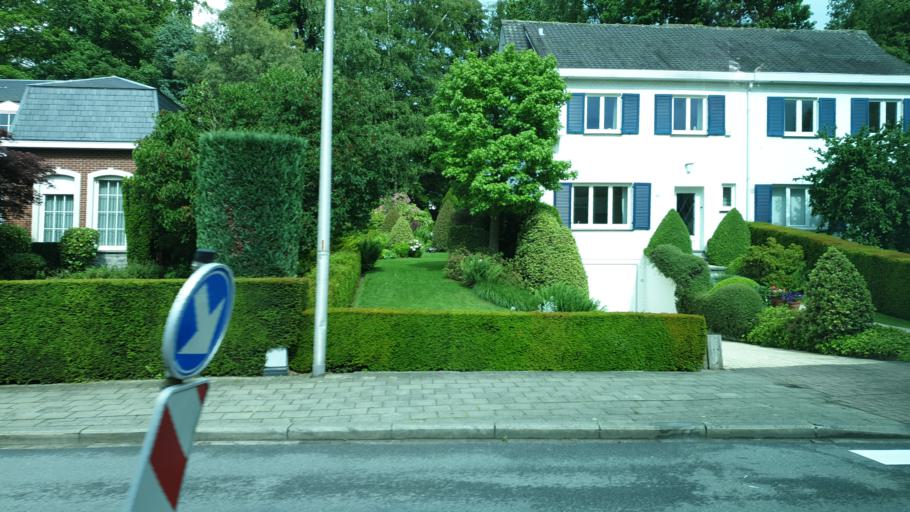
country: BE
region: Flanders
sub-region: Provincie Vlaams-Brabant
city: Wezembeek-Oppem
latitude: 50.8296
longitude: 4.4656
